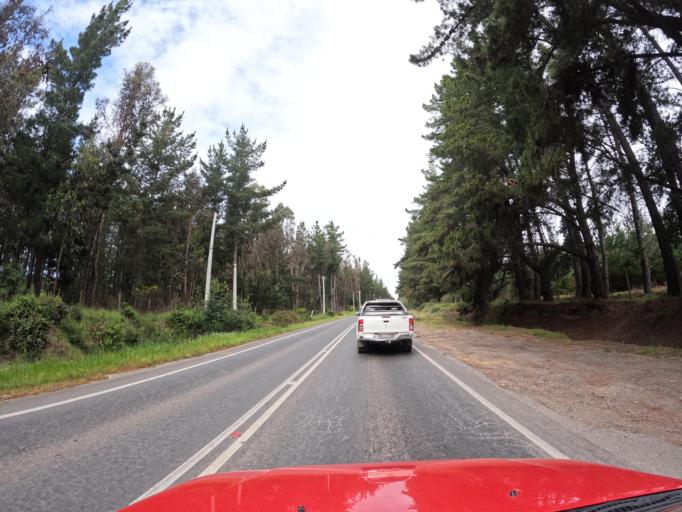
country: CL
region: O'Higgins
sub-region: Provincia de Colchagua
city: Santa Cruz
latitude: -34.3583
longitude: -71.8965
